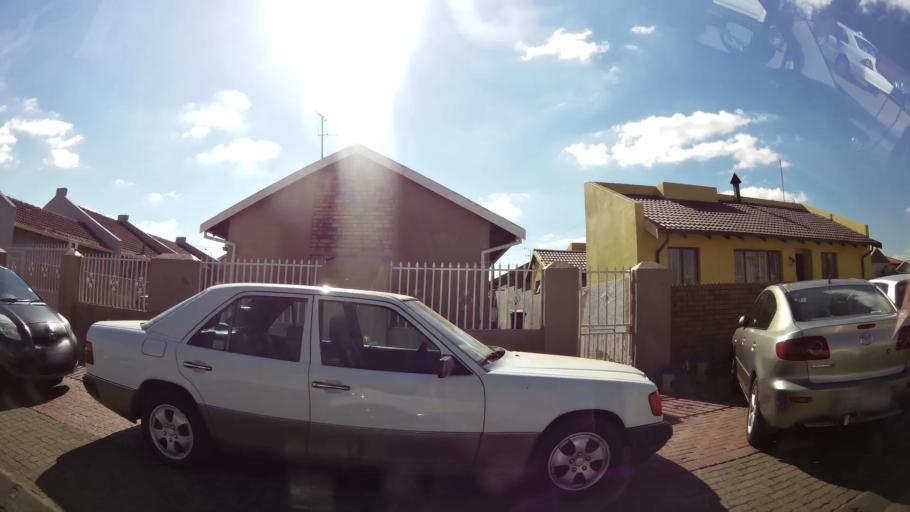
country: ZA
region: Gauteng
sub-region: West Rand District Municipality
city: Krugersdorp
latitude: -26.1529
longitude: 27.7835
